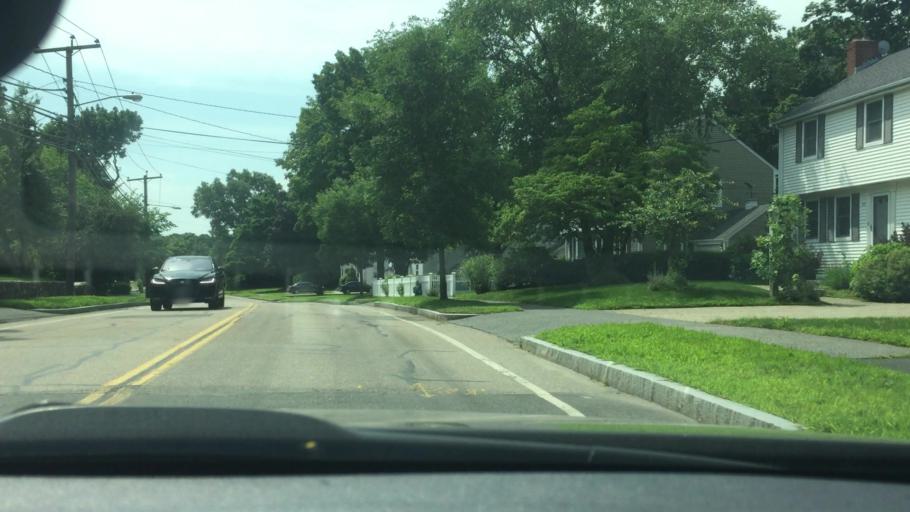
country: US
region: Massachusetts
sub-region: Norfolk County
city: Needham
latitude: 42.3053
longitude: -71.2362
